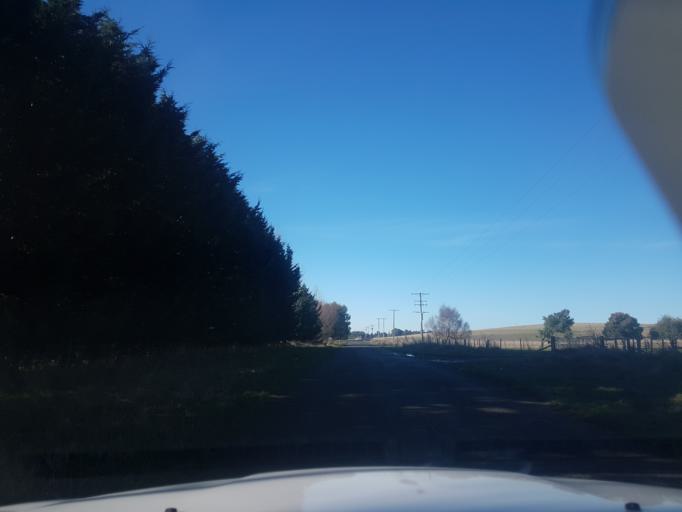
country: NZ
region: Canterbury
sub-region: Timaru District
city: Pleasant Point
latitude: -44.2905
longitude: 171.0656
